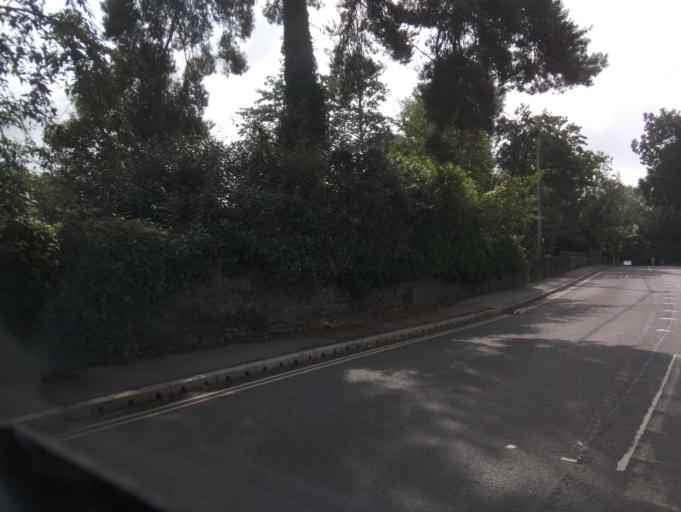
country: GB
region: England
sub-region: Somerset
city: Bruton
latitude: 51.1097
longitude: -2.4590
